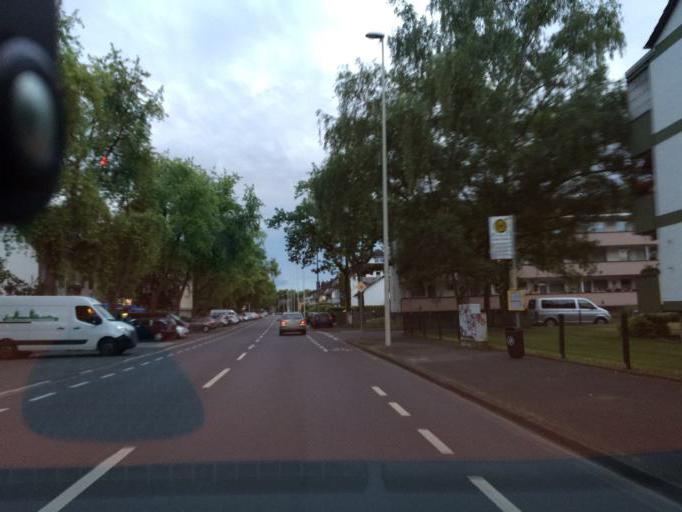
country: DE
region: North Rhine-Westphalia
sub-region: Regierungsbezirk Koln
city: Bonn
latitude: 50.6975
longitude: 7.1293
